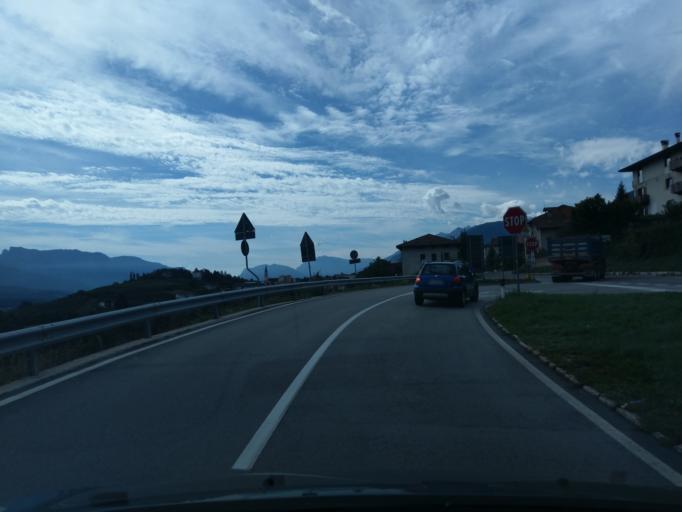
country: IT
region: Trentino-Alto Adige
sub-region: Provincia di Trento
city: Cles
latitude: 46.3753
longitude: 11.0343
